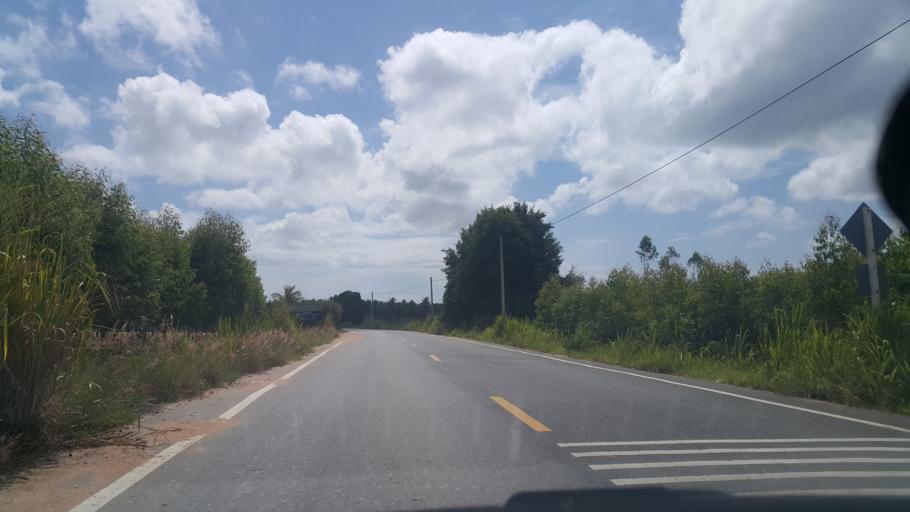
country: TH
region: Rayong
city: Ban Chang
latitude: 12.8070
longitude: 101.0117
